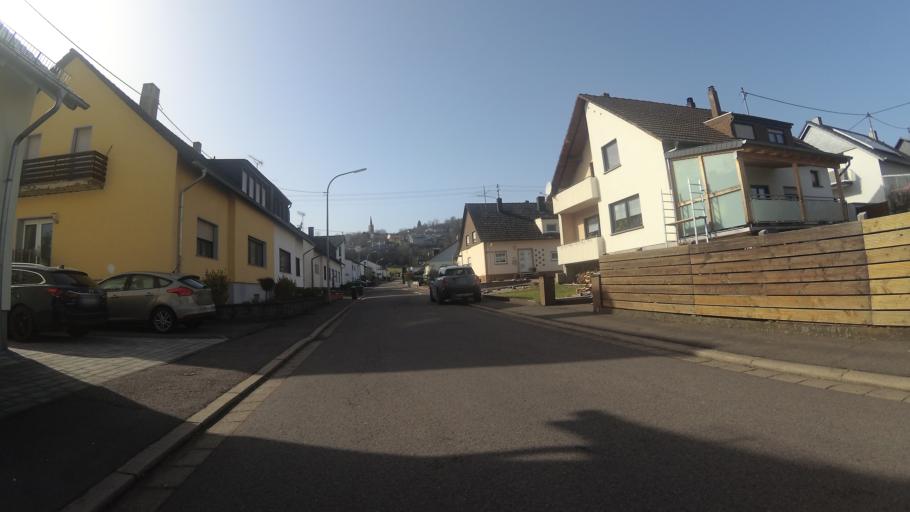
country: DE
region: Saarland
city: Wallerfangen
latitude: 49.2930
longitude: 6.6994
